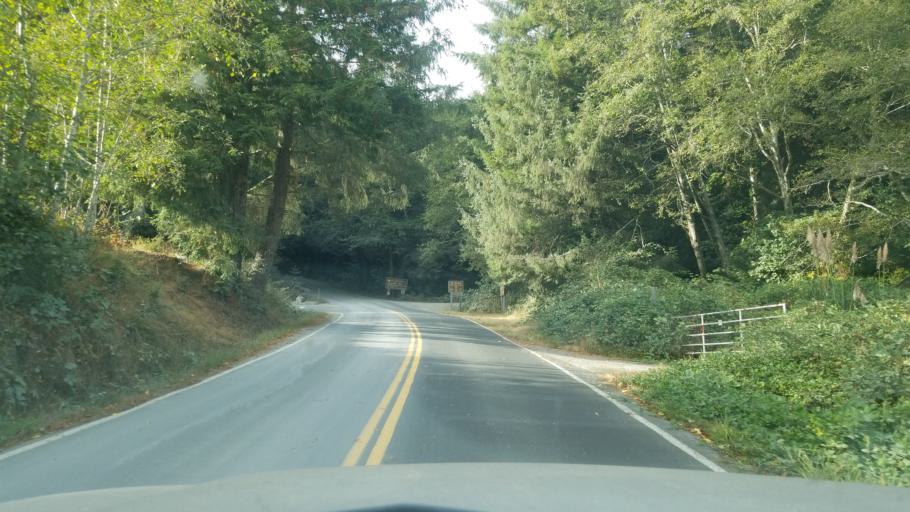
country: US
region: California
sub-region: Humboldt County
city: Westhaven-Moonstone
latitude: 41.3236
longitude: -124.0434
